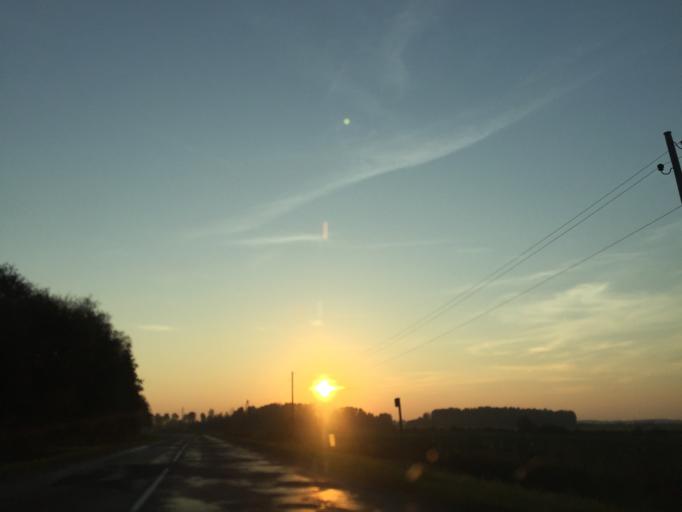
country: LT
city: Skuodas
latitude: 56.3380
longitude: 21.5663
